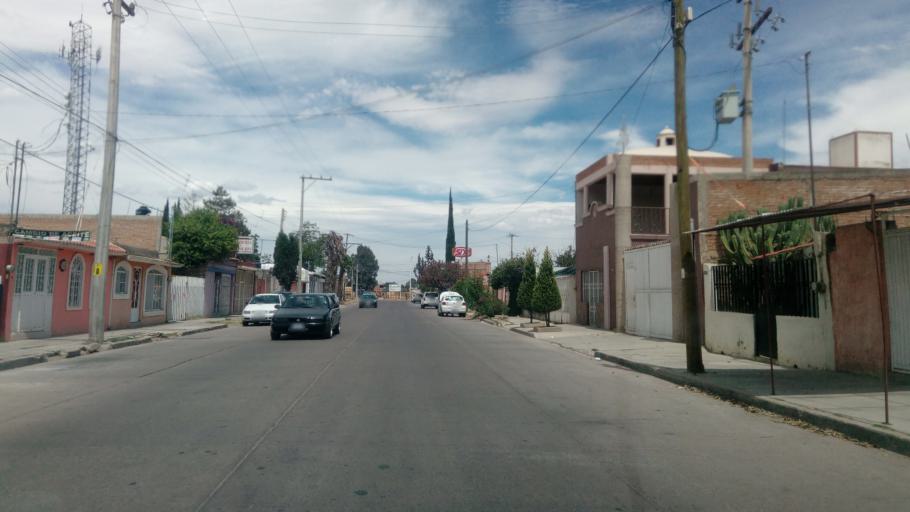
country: MX
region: Durango
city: Victoria de Durango
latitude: 23.9962
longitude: -104.6596
